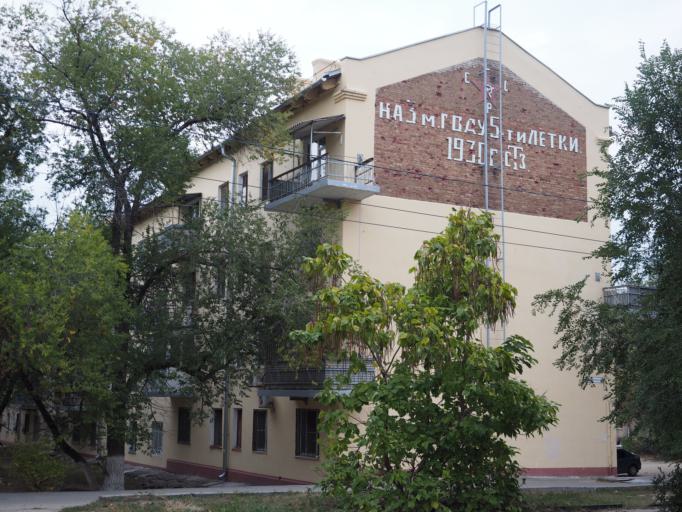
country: RU
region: Volgograd
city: Vodstroy
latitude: 48.8057
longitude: 44.5925
